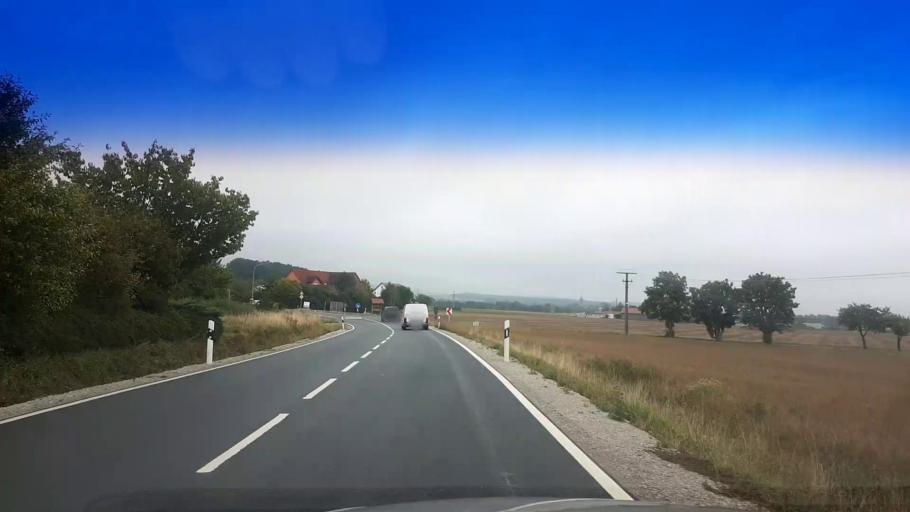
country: DE
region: Bavaria
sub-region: Upper Franconia
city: Buttenheim
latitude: 49.7876
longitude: 11.0420
